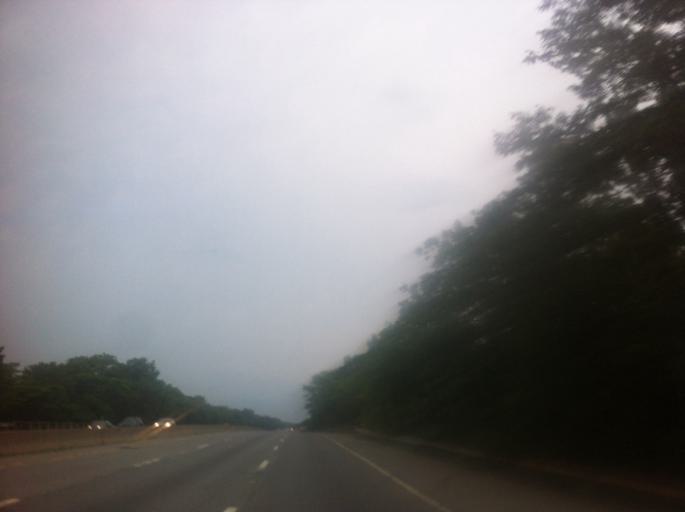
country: US
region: New York
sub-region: Nassau County
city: Bethpage
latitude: 40.7459
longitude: -73.4735
